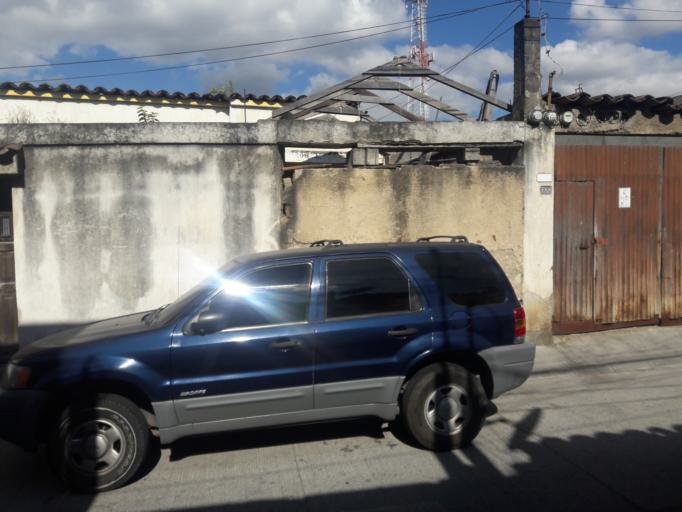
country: GT
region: Guatemala
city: Amatitlan
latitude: 14.4773
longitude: -90.6223
